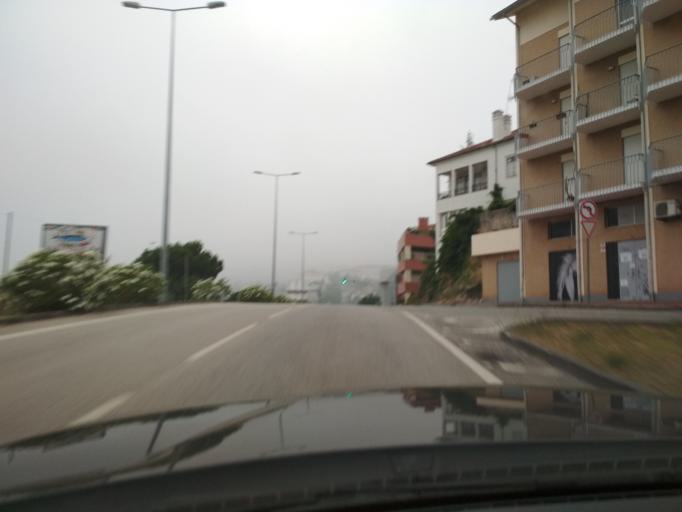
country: PT
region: Coimbra
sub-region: Coimbra
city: Coimbra
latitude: 40.1939
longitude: -8.4208
